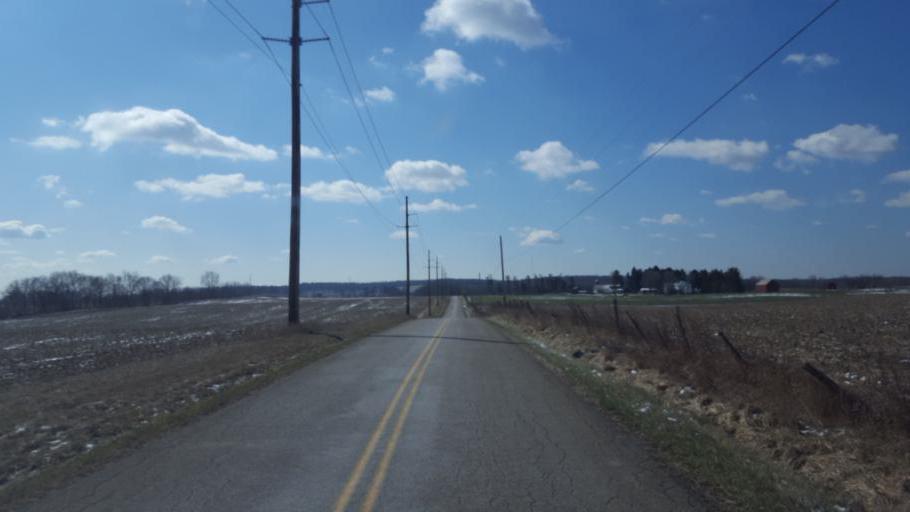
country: US
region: Ohio
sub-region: Licking County
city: Utica
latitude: 40.2723
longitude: -82.4755
